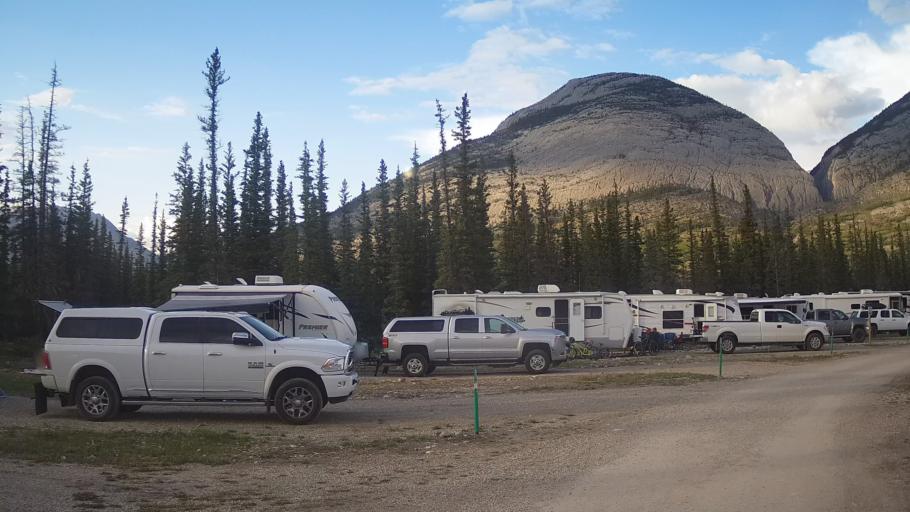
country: CA
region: Alberta
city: Jasper Park Lodge
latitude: 53.0176
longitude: -118.0859
